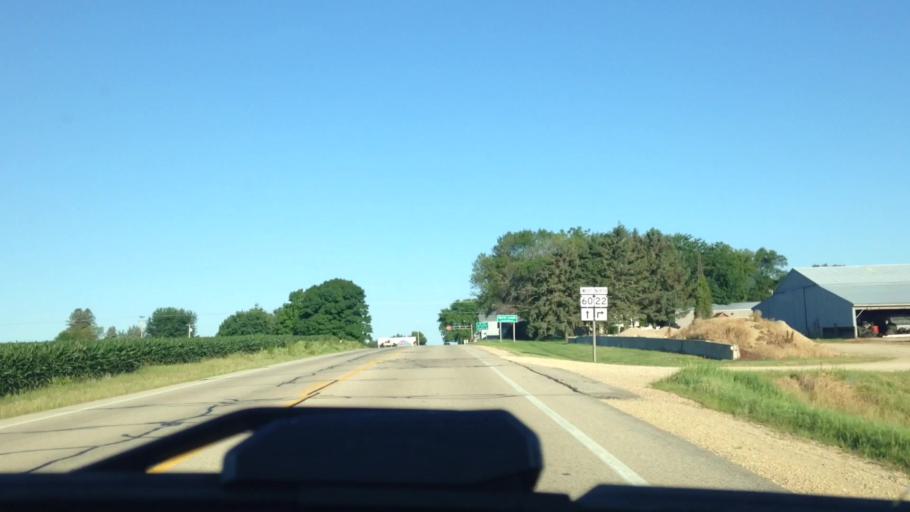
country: US
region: Wisconsin
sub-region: Dane County
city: De Forest
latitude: 43.3321
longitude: -89.3221
